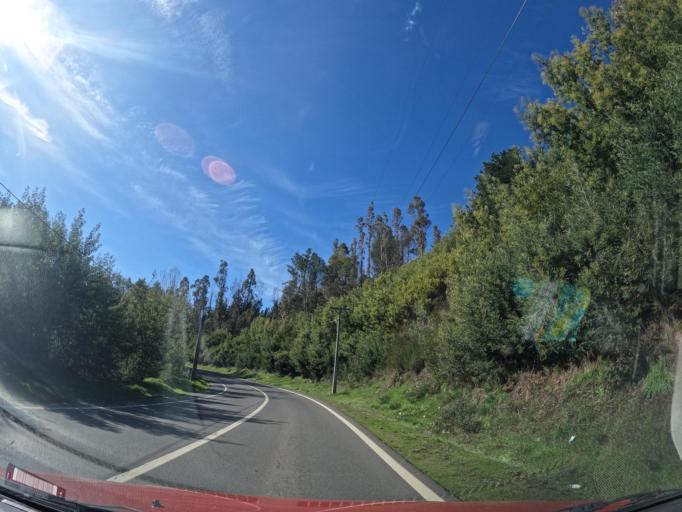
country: CL
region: Biobio
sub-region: Provincia de Concepcion
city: Penco
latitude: -36.8180
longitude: -72.8748
